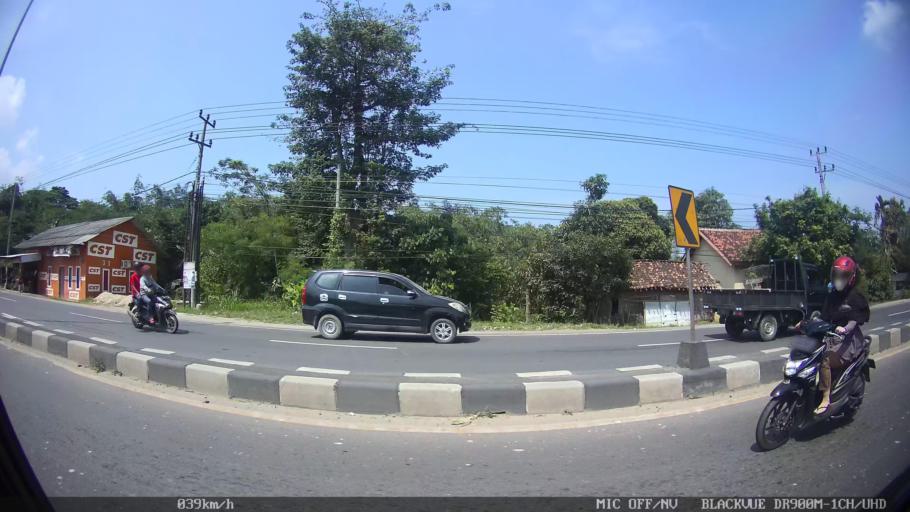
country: ID
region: Lampung
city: Natar
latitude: -5.2824
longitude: 105.1890
